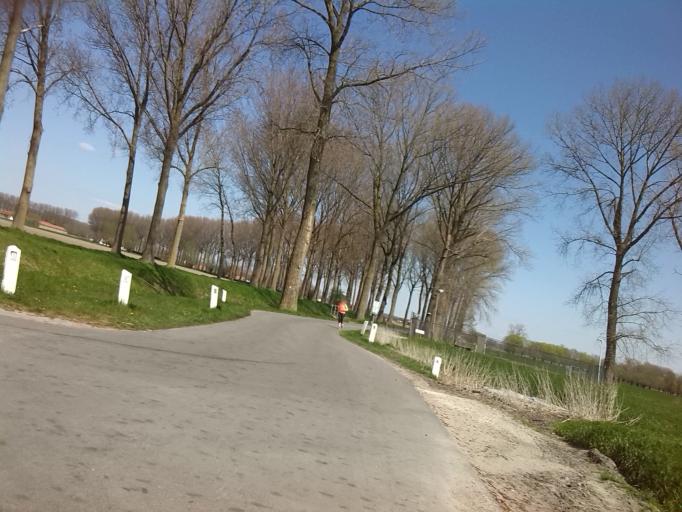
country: BE
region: Flanders
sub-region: Provincie West-Vlaanderen
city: Sint-Kruis
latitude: 51.2234
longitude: 3.2547
